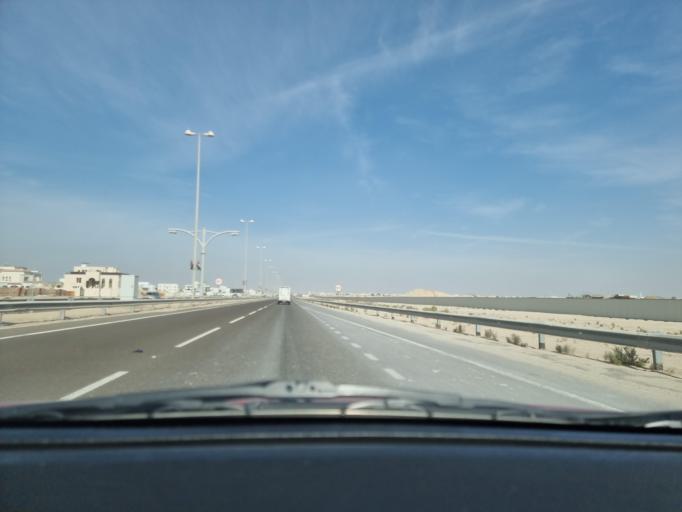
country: AE
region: Abu Dhabi
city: Abu Dhabi
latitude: 24.3700
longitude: 54.6720
